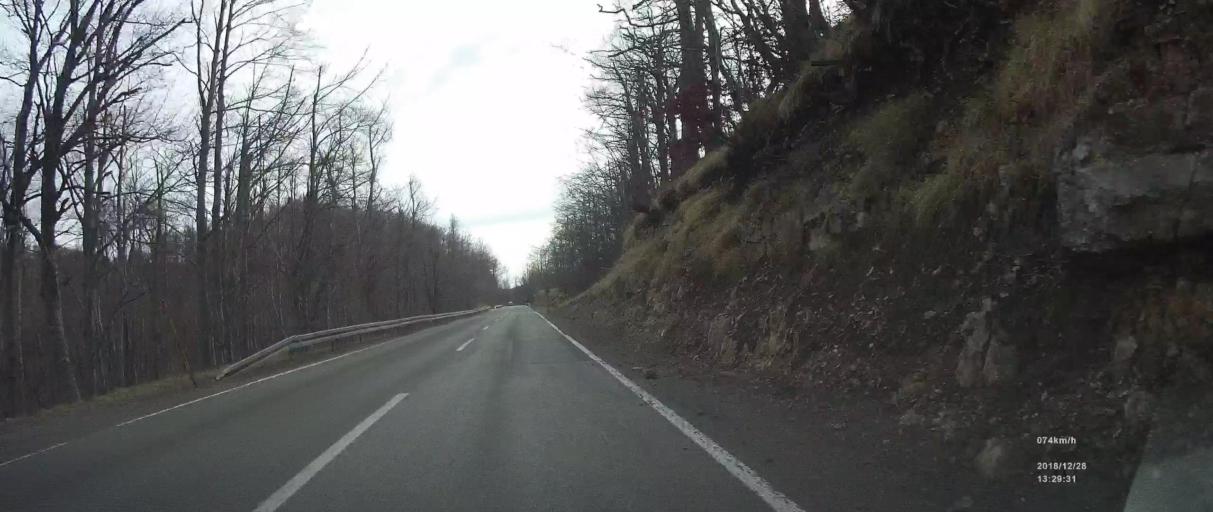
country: HR
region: Primorsko-Goranska
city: Hreljin
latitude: 45.3603
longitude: 14.6292
